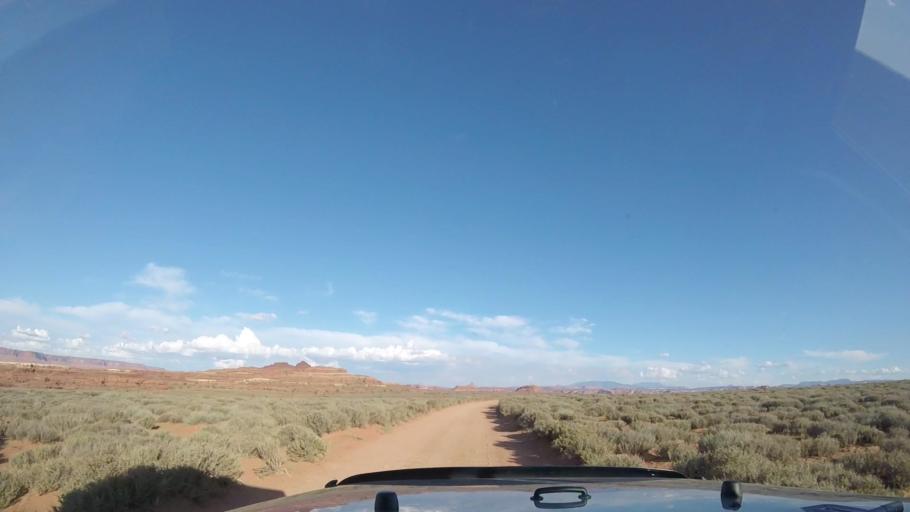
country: US
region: Utah
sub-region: Grand County
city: Moab
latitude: 38.2142
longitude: -109.7920
